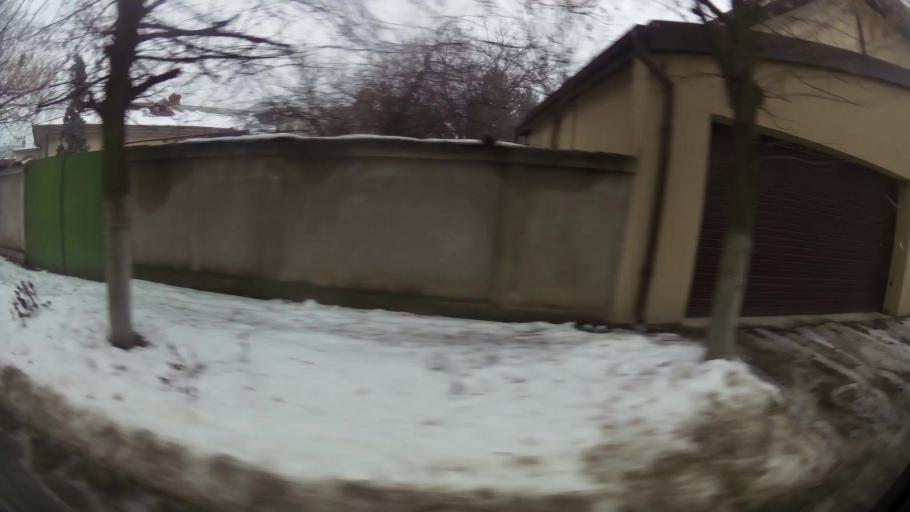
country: RO
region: Ilfov
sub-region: Comuna Chiajna
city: Chiajna
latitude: 44.4574
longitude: 25.9707
